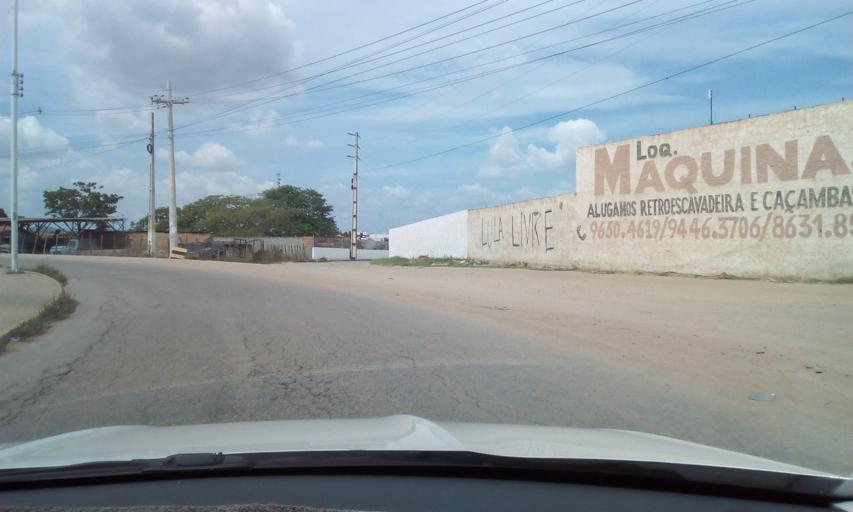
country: BR
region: Pernambuco
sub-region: Bezerros
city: Bezerros
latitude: -8.2481
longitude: -35.7580
